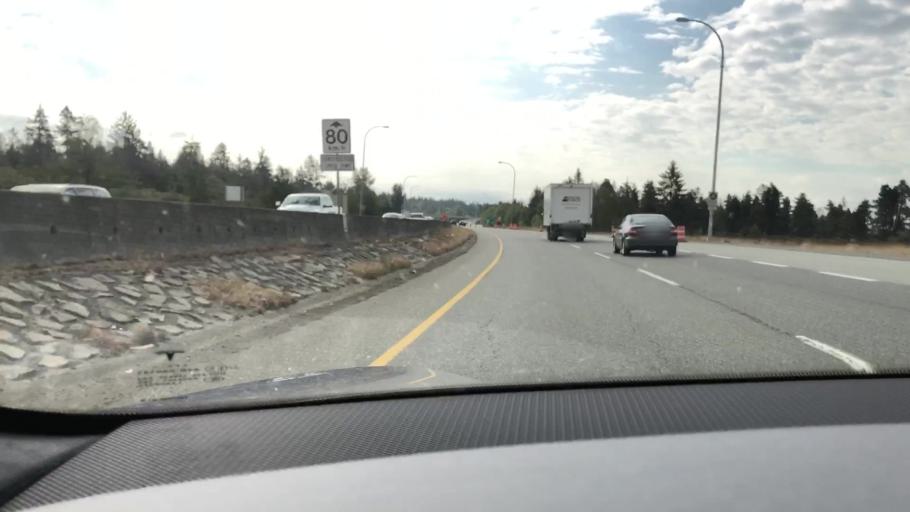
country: CA
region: British Columbia
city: Delta
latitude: 49.1408
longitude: -122.9350
